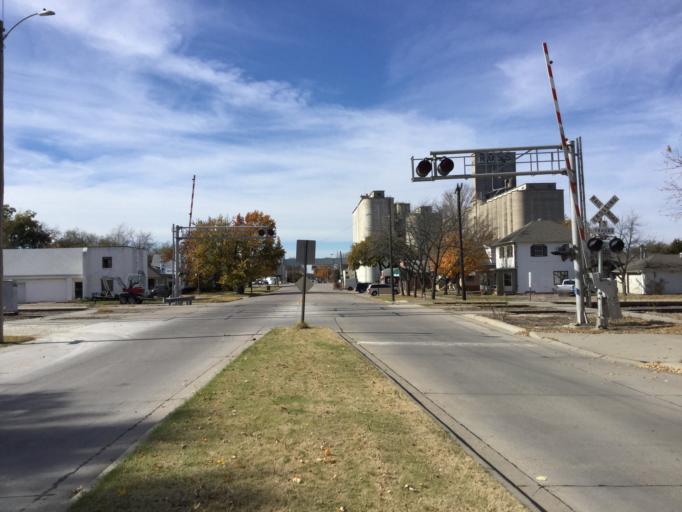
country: US
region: Kansas
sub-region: Harvey County
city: Newton
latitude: 38.0499
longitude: -97.3364
